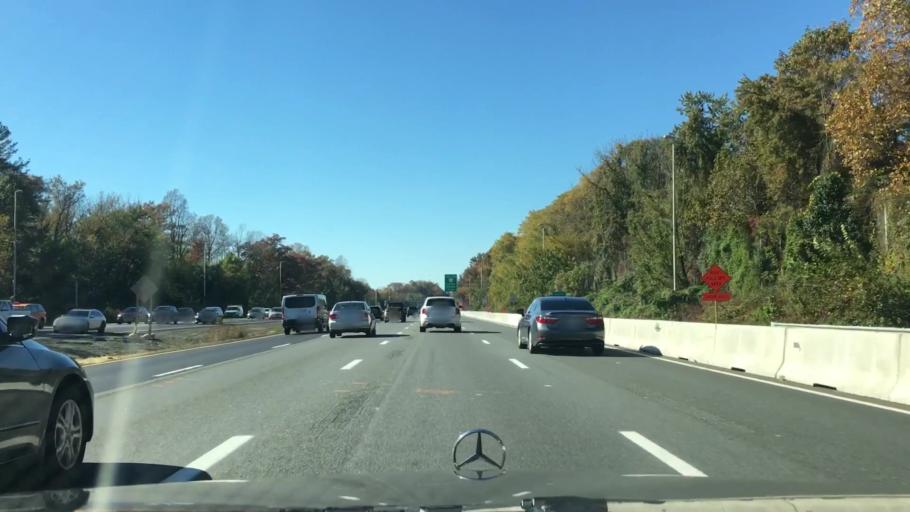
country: US
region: Virginia
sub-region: Fairfax County
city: Oakton
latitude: 38.8719
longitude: -77.2828
